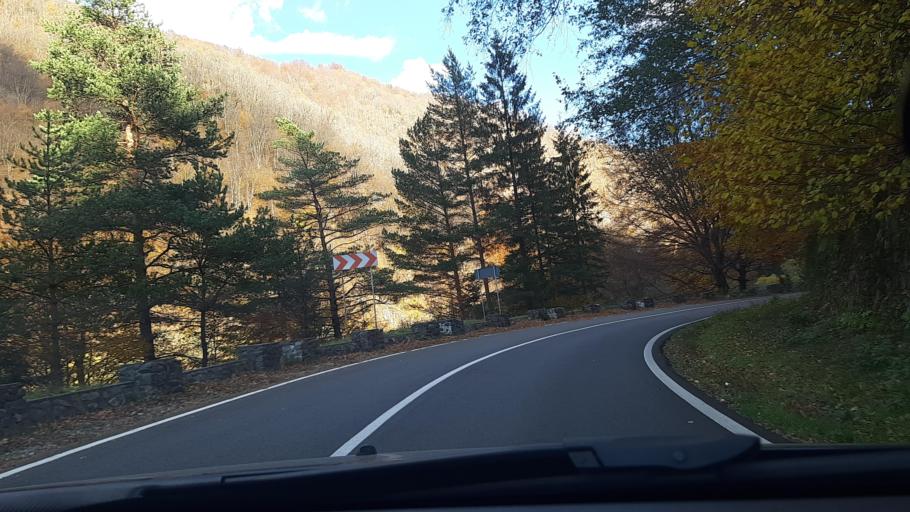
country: RO
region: Valcea
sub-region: Comuna Voineasa
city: Voineasa
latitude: 45.4074
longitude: 23.9809
